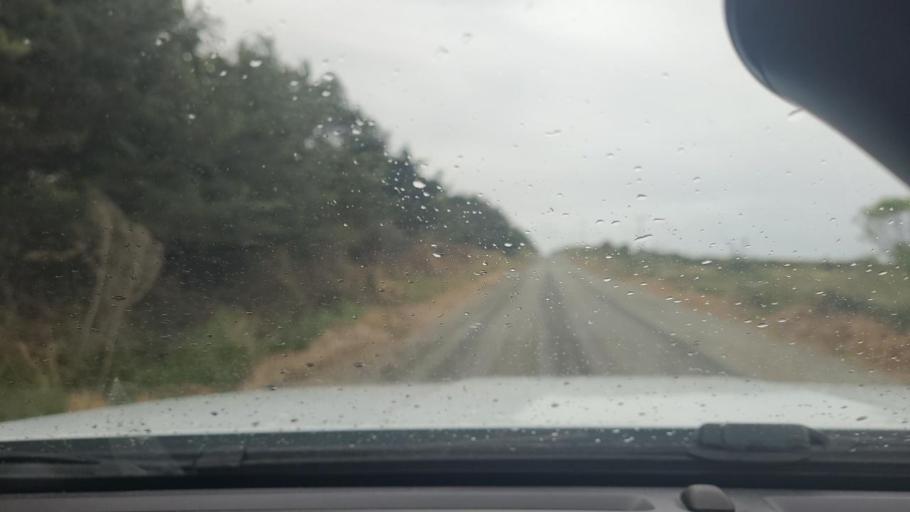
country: NZ
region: Southland
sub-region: Invercargill City
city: Invercargill
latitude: -46.3596
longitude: 168.1963
